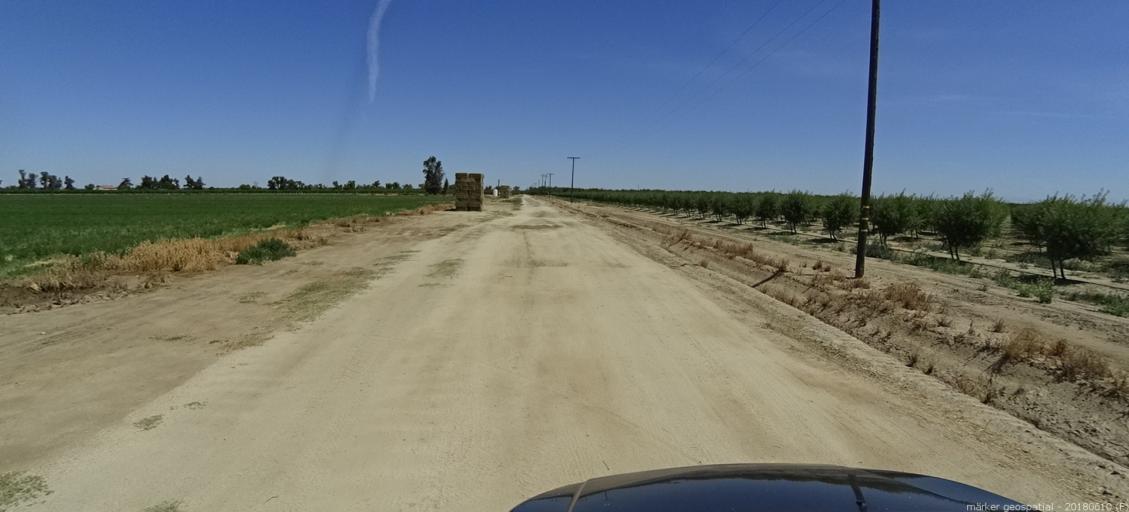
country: US
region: California
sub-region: Madera County
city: Chowchilla
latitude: 37.0405
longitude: -120.4194
